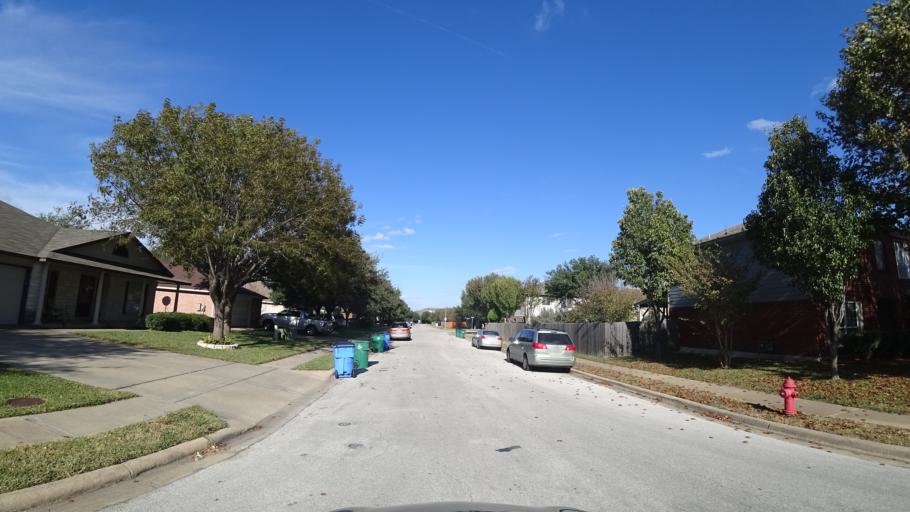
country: US
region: Texas
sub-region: Travis County
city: Wells Branch
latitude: 30.4632
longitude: -97.6875
